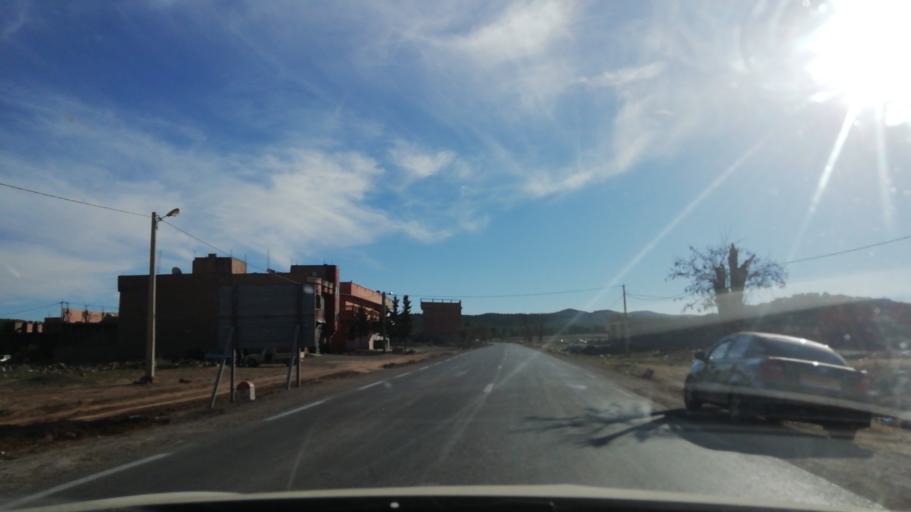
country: DZ
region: Tlemcen
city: Sebdou
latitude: 34.6232
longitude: -1.3343
